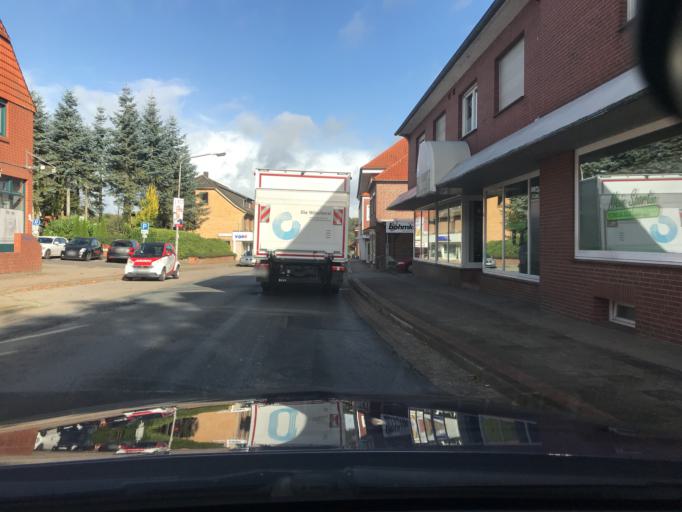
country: DE
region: Lower Saxony
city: Harsefeld
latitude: 53.4537
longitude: 9.4999
